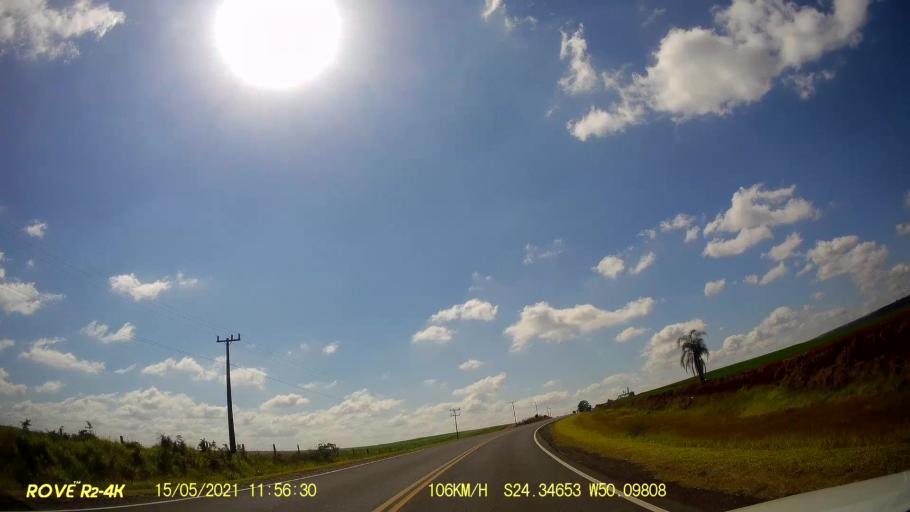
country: BR
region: Parana
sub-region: Pirai Do Sul
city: Pirai do Sul
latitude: -24.3467
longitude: -50.0981
